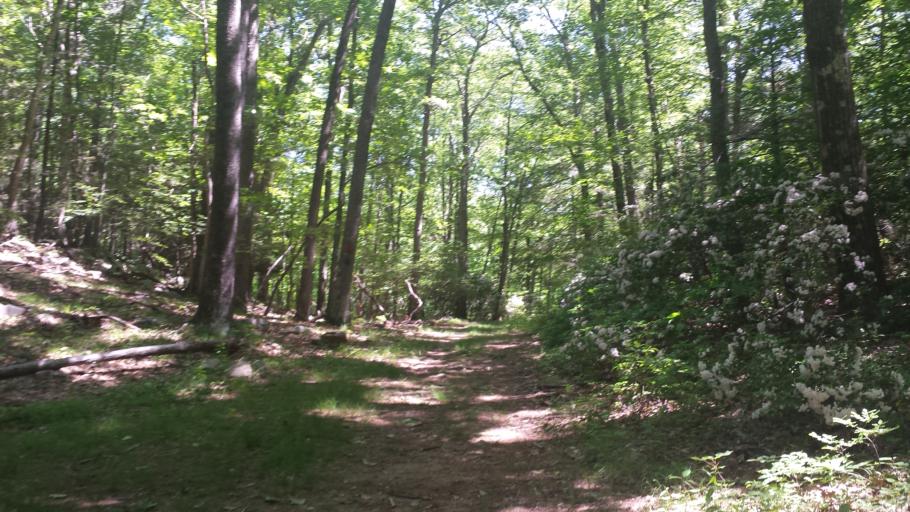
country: US
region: New York
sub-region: Westchester County
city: Pound Ridge
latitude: 41.2361
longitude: -73.5885
